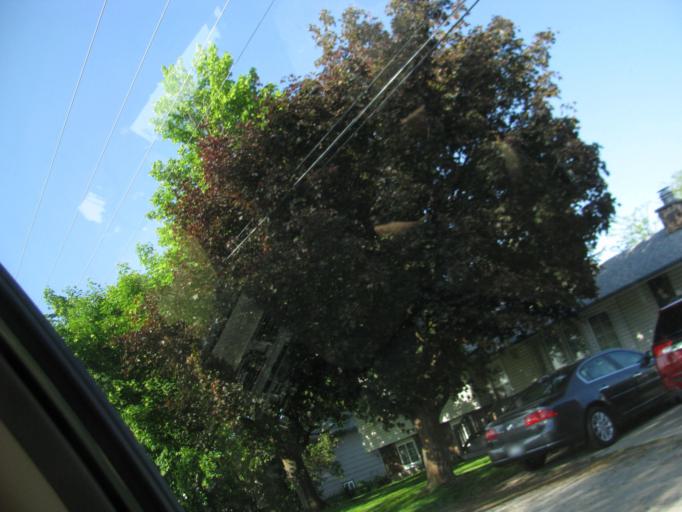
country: US
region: Washington
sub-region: Spokane County
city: Liberty Lake
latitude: 47.6539
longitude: -117.1537
